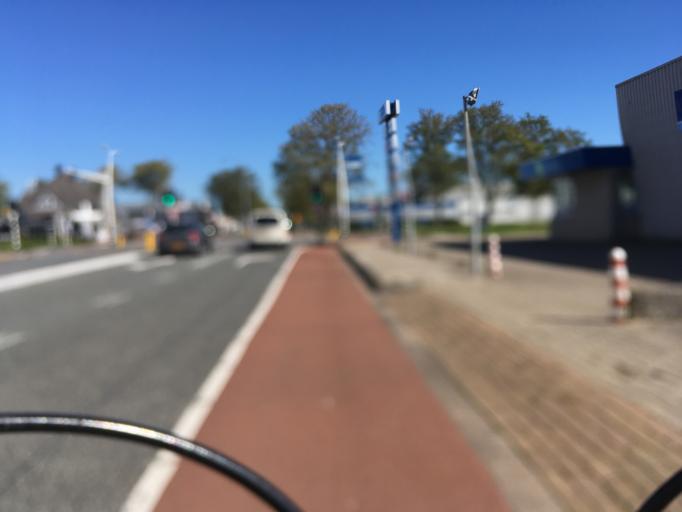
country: NL
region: North Holland
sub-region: Gemeente Haarlem
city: Haarlem
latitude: 52.3902
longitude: 4.6619
